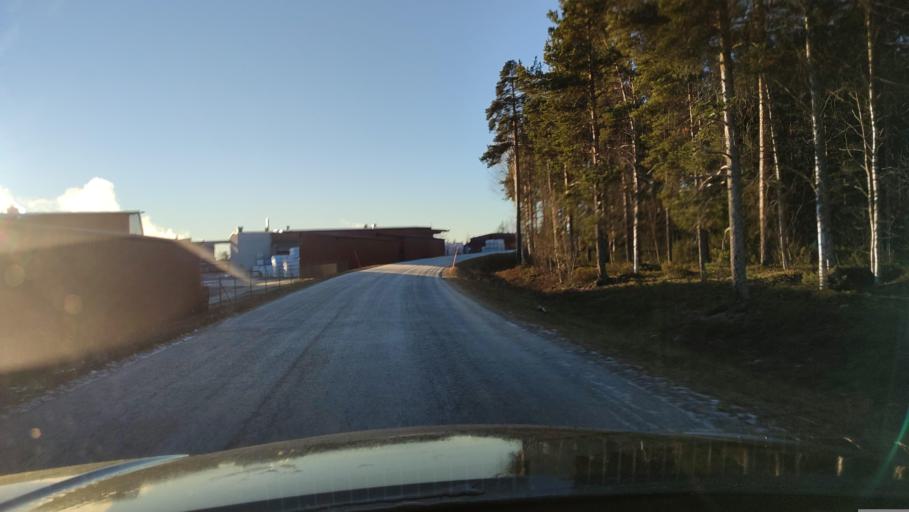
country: SE
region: Vaesterbotten
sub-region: Skelleftea Kommun
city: Viken
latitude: 64.7044
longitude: 20.9049
